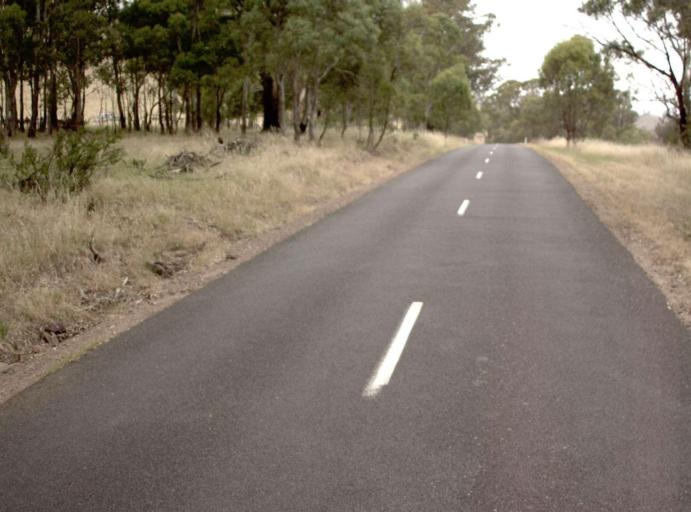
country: AU
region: Victoria
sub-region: Wellington
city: Heyfield
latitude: -37.6733
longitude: 146.6534
